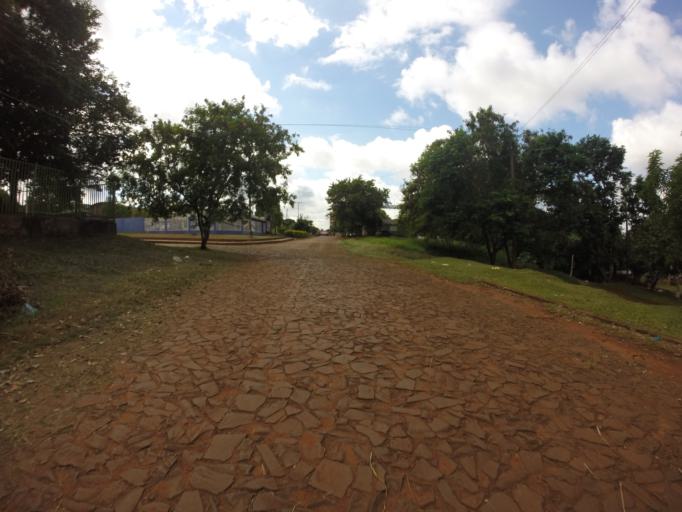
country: PY
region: Alto Parana
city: Ciudad del Este
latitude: -25.3948
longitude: -54.6417
